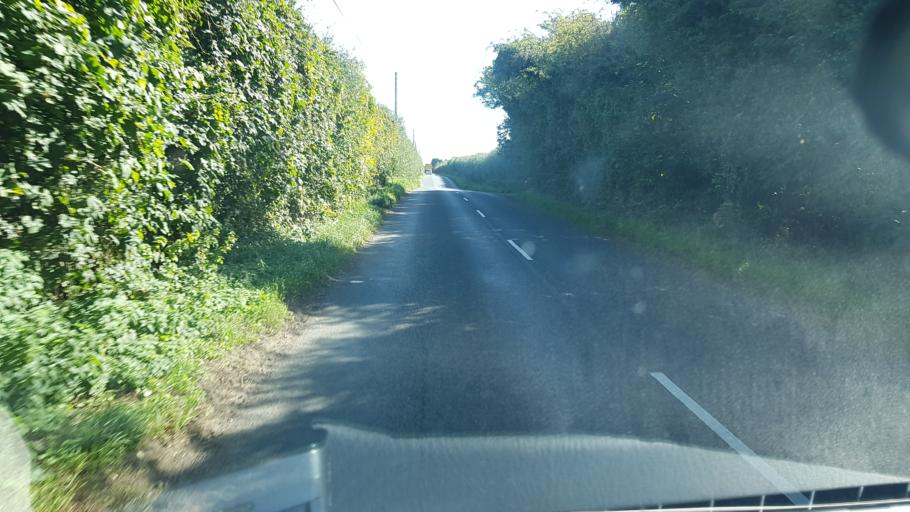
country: GB
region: England
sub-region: Kent
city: Yalding
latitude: 51.2390
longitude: 0.4675
